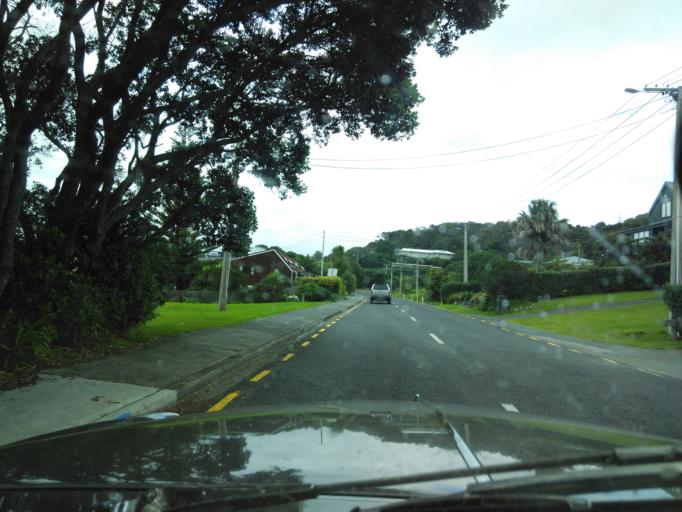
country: NZ
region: Auckland
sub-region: Auckland
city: Wellsford
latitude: -36.0807
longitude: 174.5955
